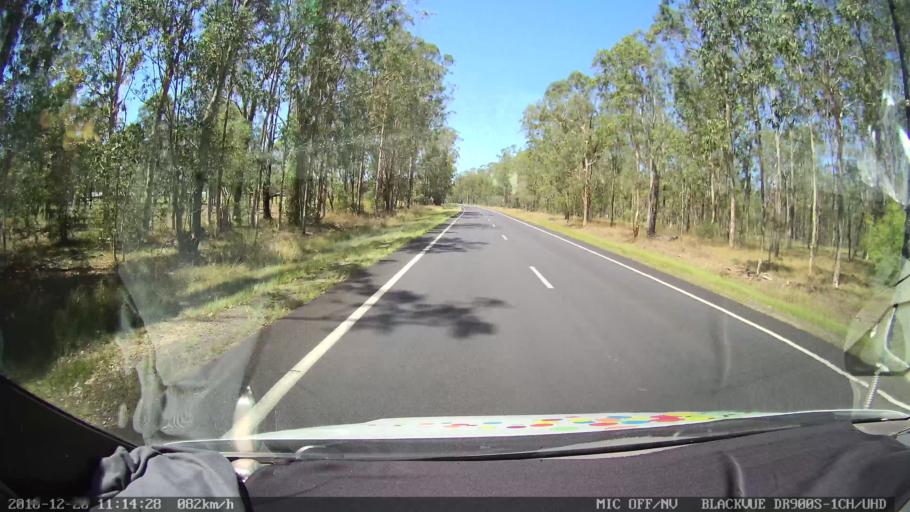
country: AU
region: New South Wales
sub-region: Richmond Valley
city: Casino
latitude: -29.0008
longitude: 153.0086
